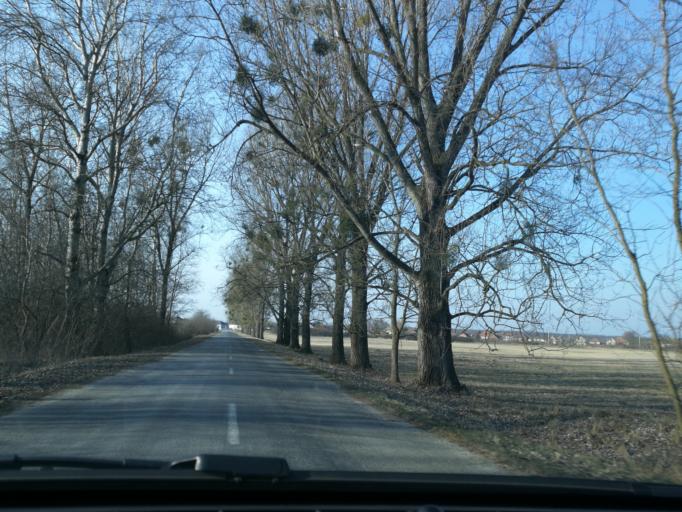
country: HU
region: Szabolcs-Szatmar-Bereg
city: Levelek
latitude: 48.0278
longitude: 21.9652
